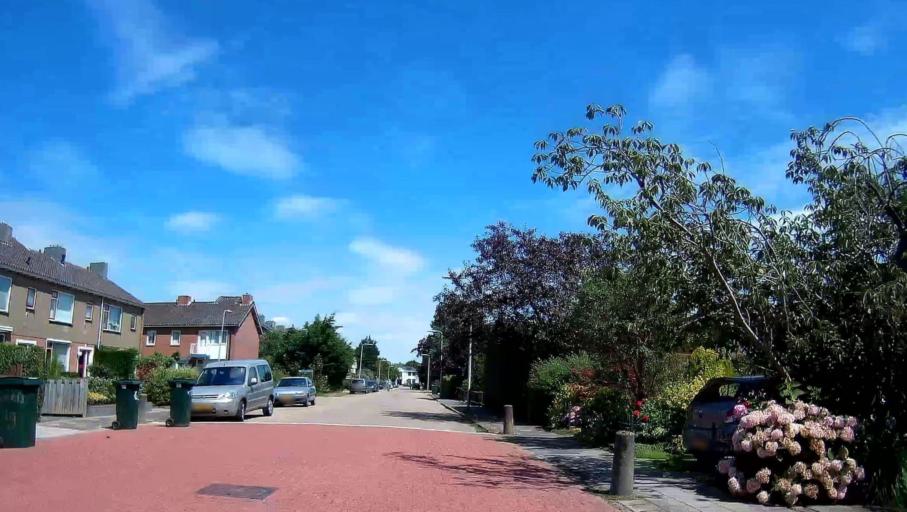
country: NL
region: South Holland
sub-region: Gemeente Krimpen aan den IJssel
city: Krimpen aan den IJssel
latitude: 51.9093
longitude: 4.5991
